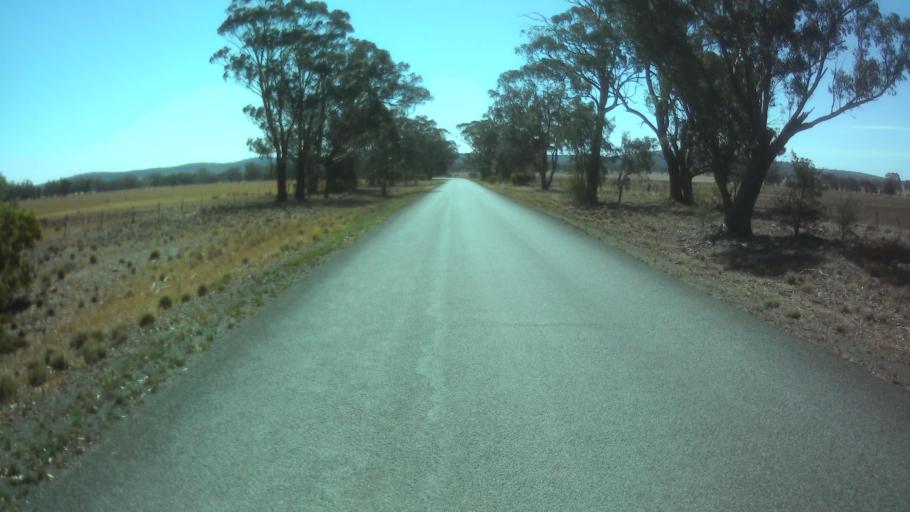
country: AU
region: New South Wales
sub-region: Weddin
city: Grenfell
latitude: -33.8103
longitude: 147.9143
